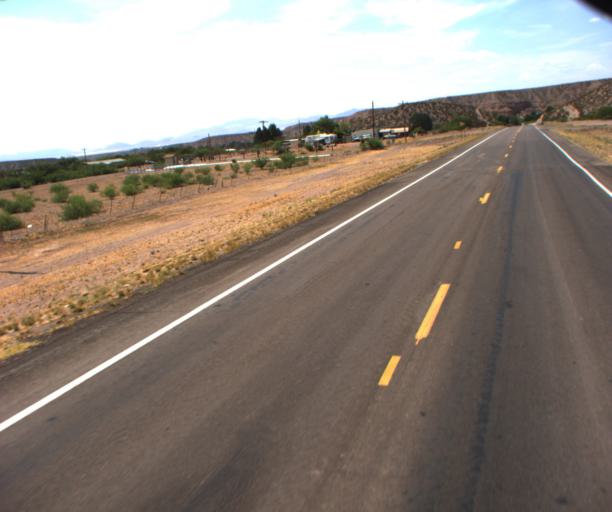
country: US
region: Arizona
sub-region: Greenlee County
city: Clifton
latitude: 32.9211
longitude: -109.1988
